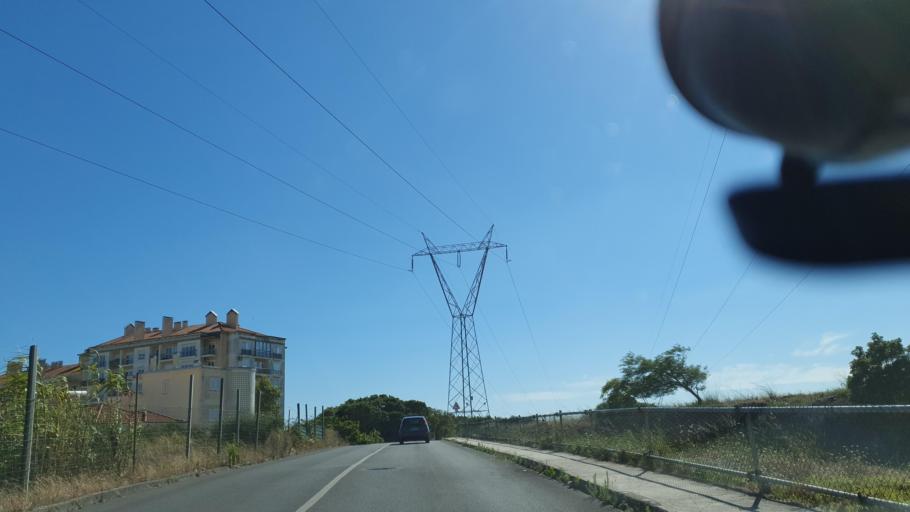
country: PT
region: Lisbon
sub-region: Sintra
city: Cacem
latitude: 38.7612
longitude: -9.2816
